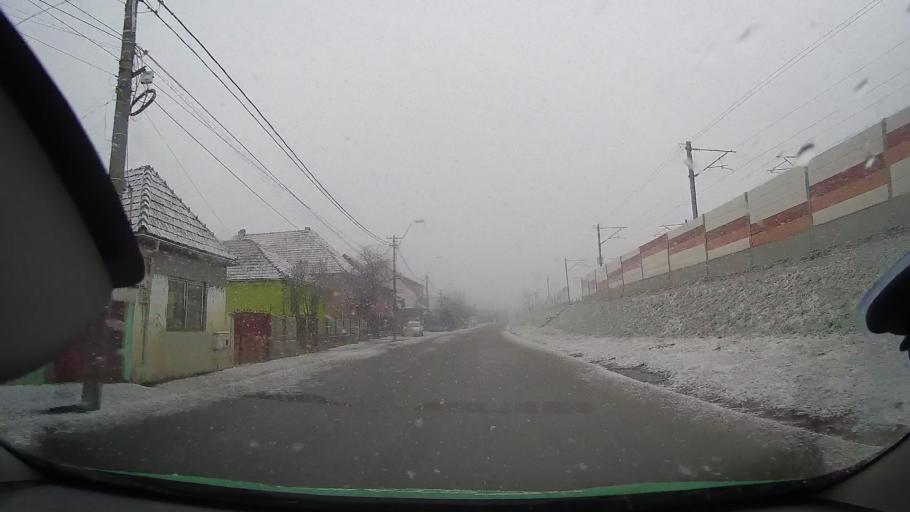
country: RO
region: Sibiu
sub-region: Municipiul Medias
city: Medias
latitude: 46.1644
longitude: 24.3659
